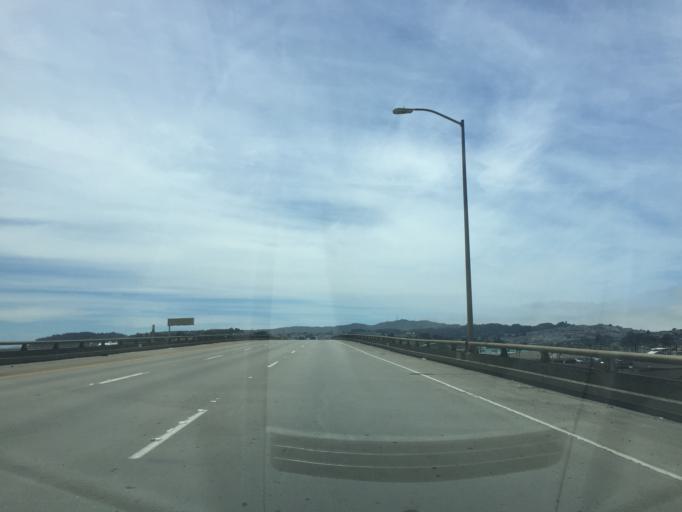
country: US
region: California
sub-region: San Francisco County
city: San Francisco
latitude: 37.7495
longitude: -122.3927
